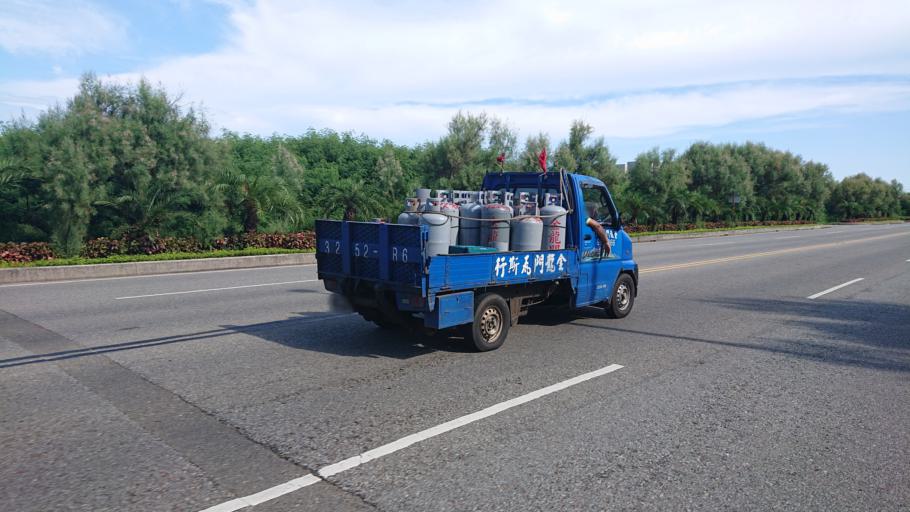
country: TW
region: Taiwan
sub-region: Penghu
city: Ma-kung
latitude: 23.5368
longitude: 119.6034
